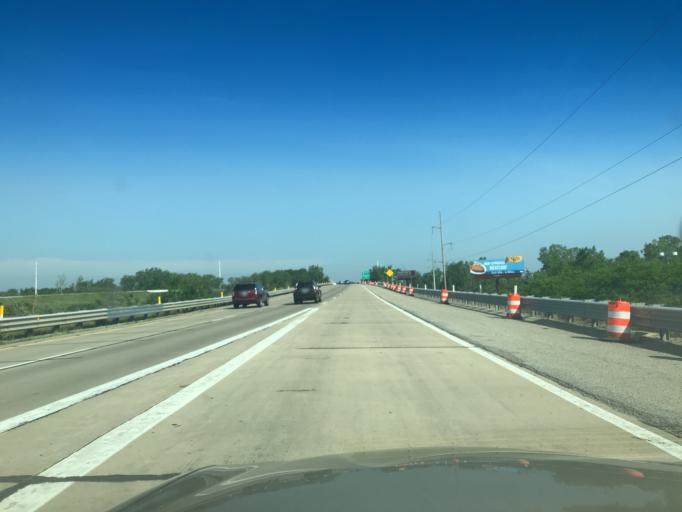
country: US
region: Michigan
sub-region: Eaton County
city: Dimondale
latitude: 42.6806
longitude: -84.6555
